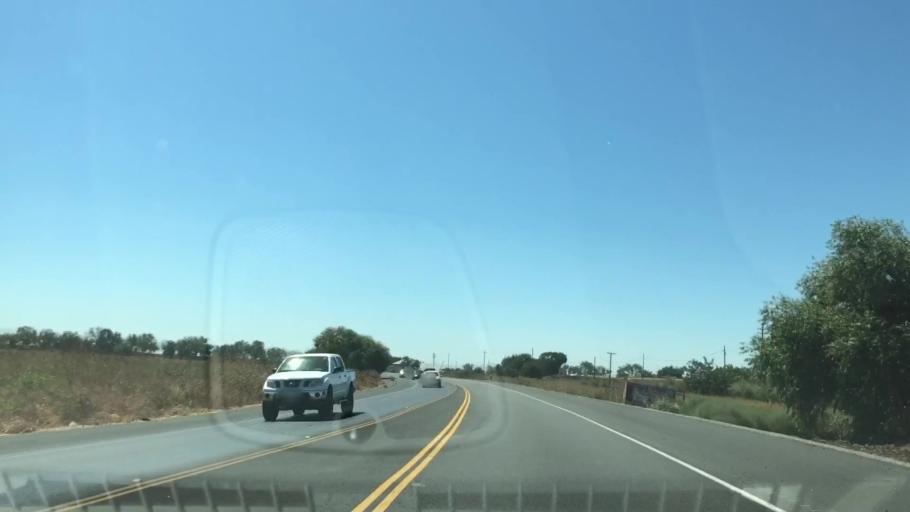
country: US
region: California
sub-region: San Joaquin County
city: Country Club
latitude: 37.9264
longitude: -121.4317
